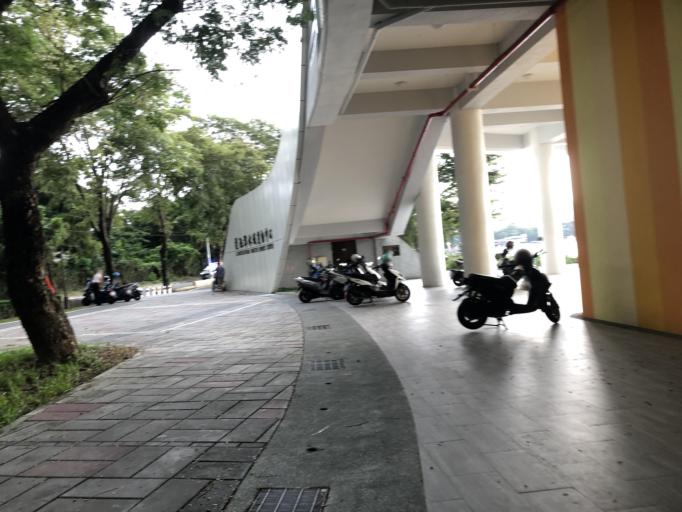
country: TW
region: Kaohsiung
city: Kaohsiung
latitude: 22.6828
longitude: 120.2983
